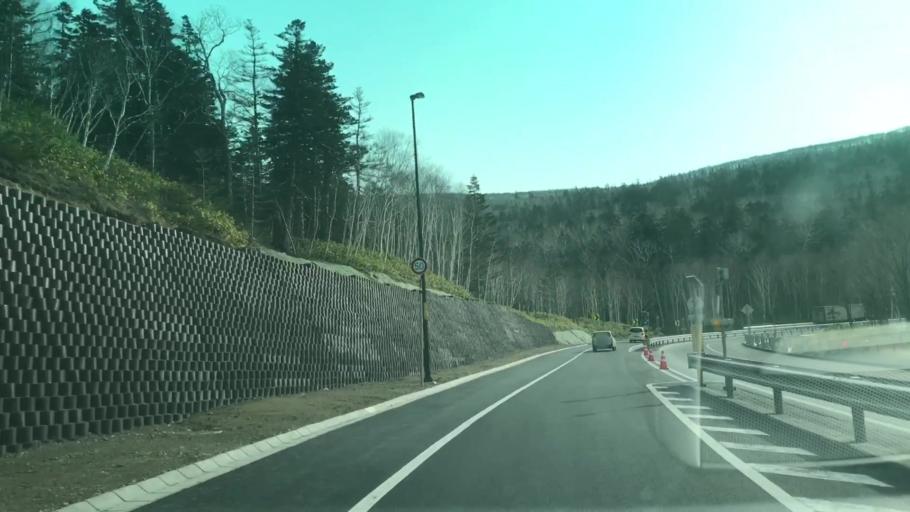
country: JP
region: Hokkaido
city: Otofuke
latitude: 42.9834
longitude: 142.7541
